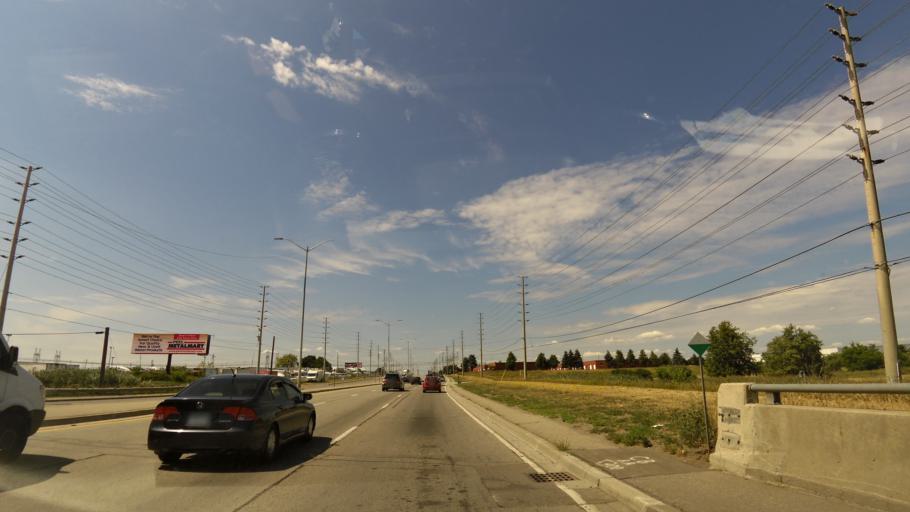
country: CA
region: Ontario
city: Brampton
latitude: 43.6785
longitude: -79.6788
